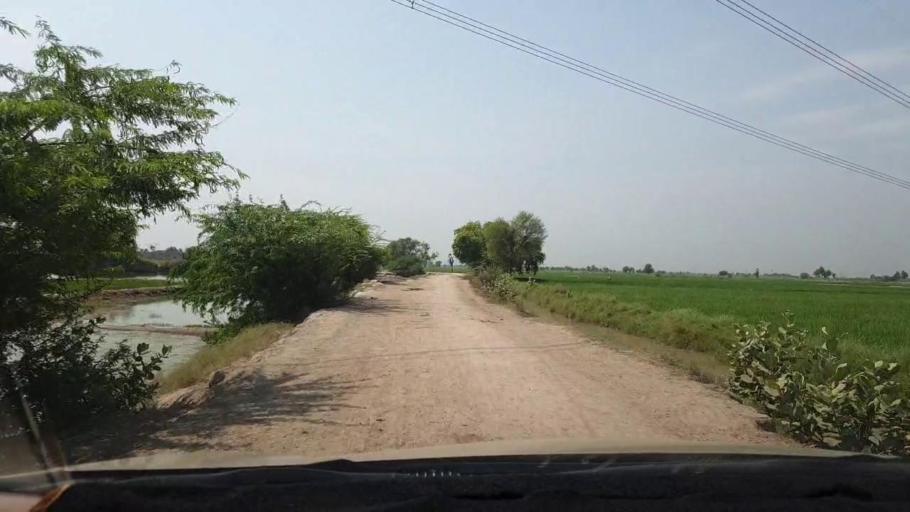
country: PK
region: Sindh
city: Naudero
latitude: 27.6538
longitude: 68.2596
